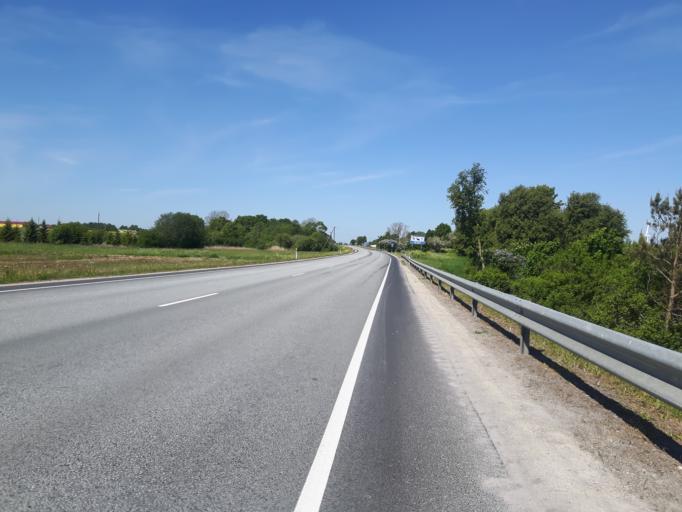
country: EE
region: Ida-Virumaa
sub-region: Aseri vald
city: Aseri
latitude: 59.4377
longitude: 26.8625
